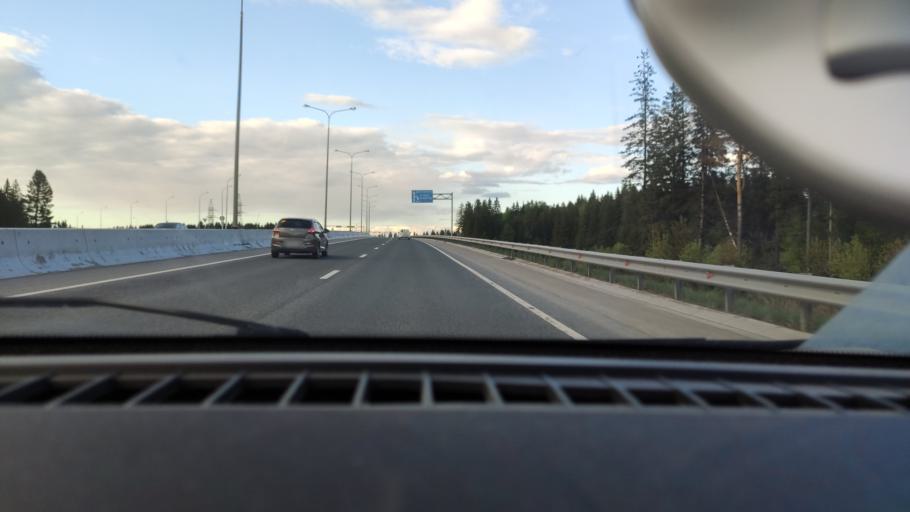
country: RU
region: Perm
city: Ferma
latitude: 57.9474
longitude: 56.3843
